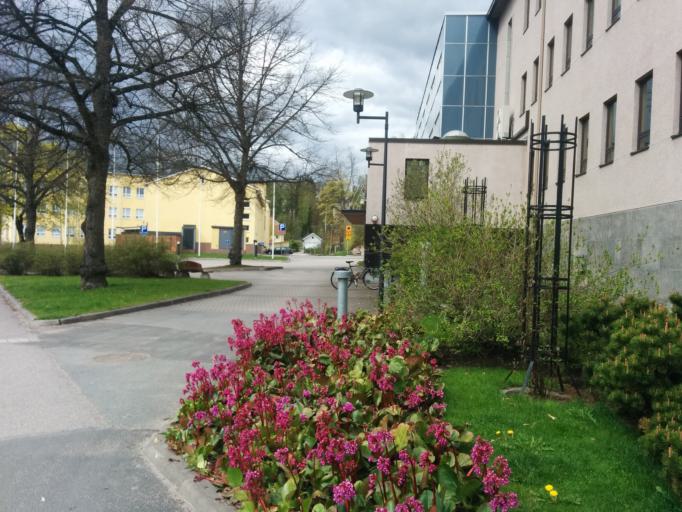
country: FI
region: Haeme
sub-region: Riihimaeki
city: Riihimaeki
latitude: 60.7391
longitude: 24.7696
